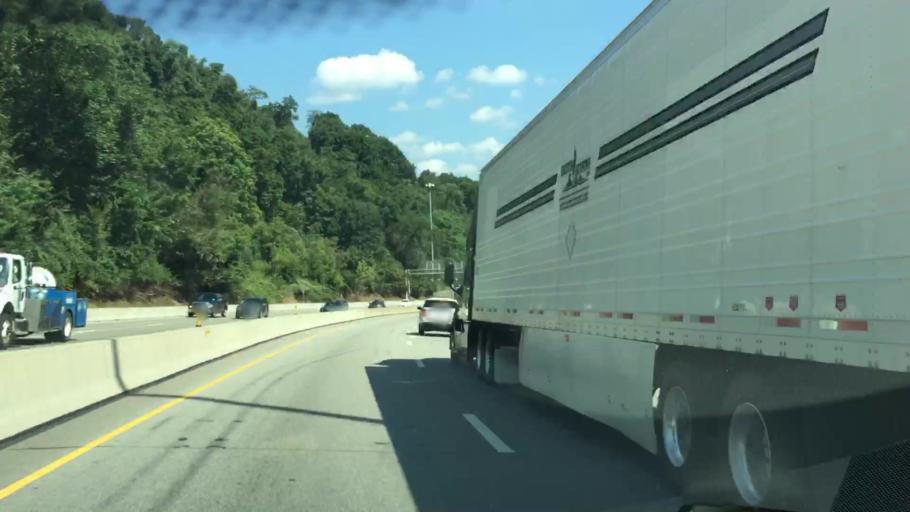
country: US
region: Pennsylvania
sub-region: Allegheny County
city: Green Tree
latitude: 40.4217
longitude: -80.0329
